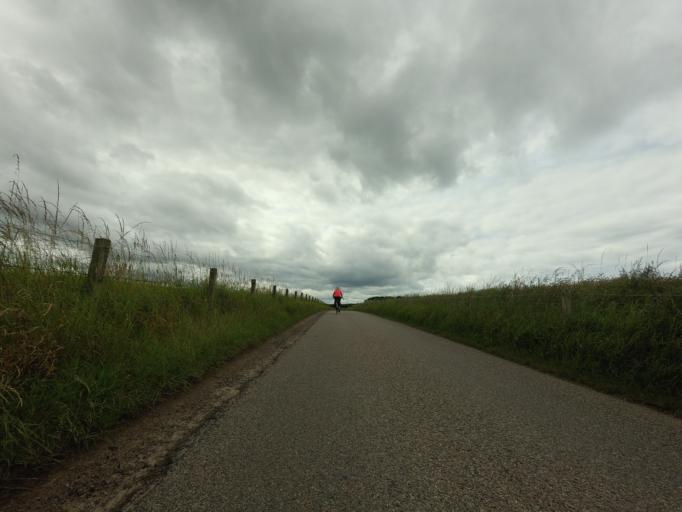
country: GB
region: Scotland
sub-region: Moray
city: Forres
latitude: 57.6219
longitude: -3.6616
